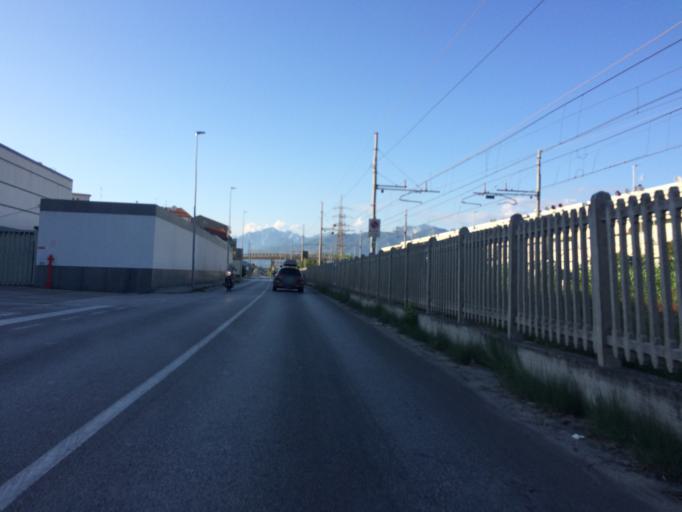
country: IT
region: Tuscany
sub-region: Provincia di Lucca
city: Viareggio
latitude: 43.8792
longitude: 10.2514
